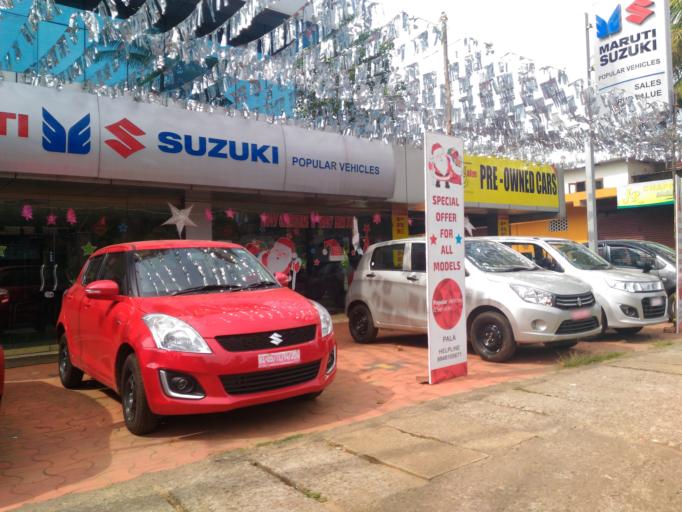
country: IN
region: Kerala
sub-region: Kottayam
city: Lalam
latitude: 9.7057
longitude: 76.6694
